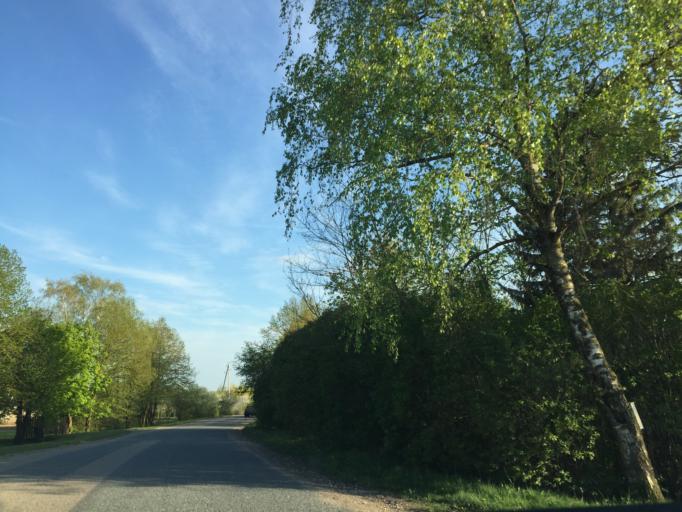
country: LV
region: Bauskas Rajons
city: Bauska
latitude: 56.3075
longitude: 24.2607
